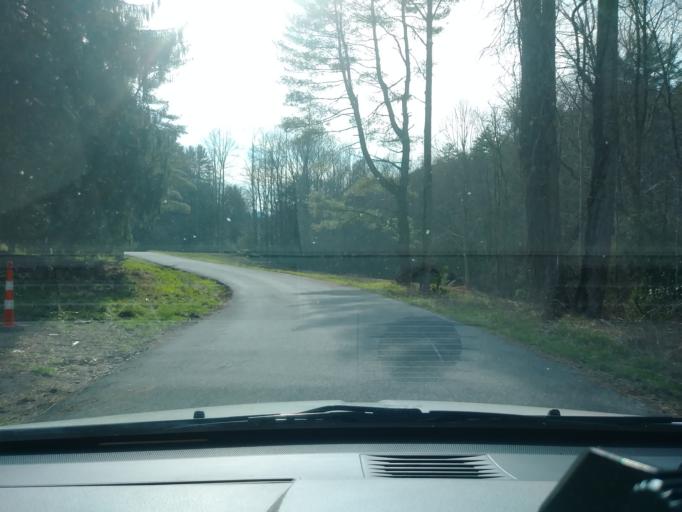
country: US
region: Tennessee
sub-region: Greene County
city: Tusculum
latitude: 36.0235
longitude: -82.7400
